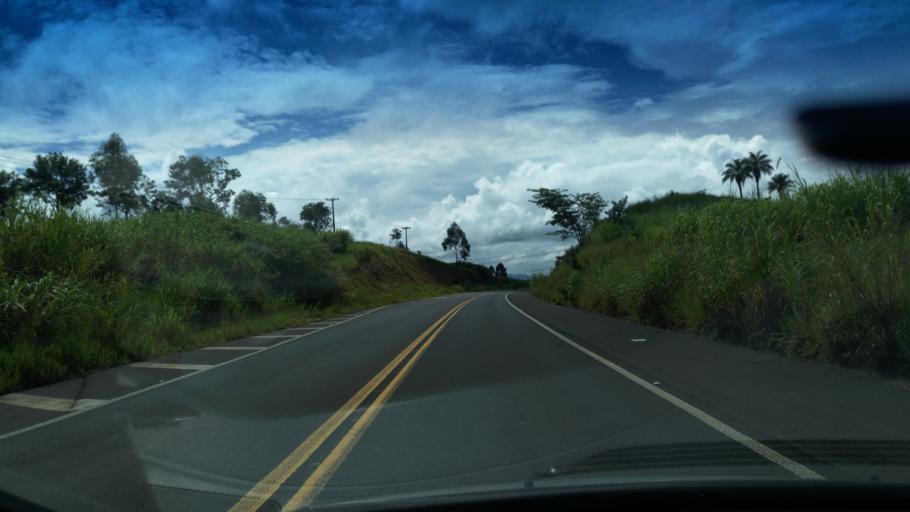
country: BR
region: Sao Paulo
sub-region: Santo Antonio Do Jardim
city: Espirito Santo do Pinhal
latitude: -22.1410
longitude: -46.7112
